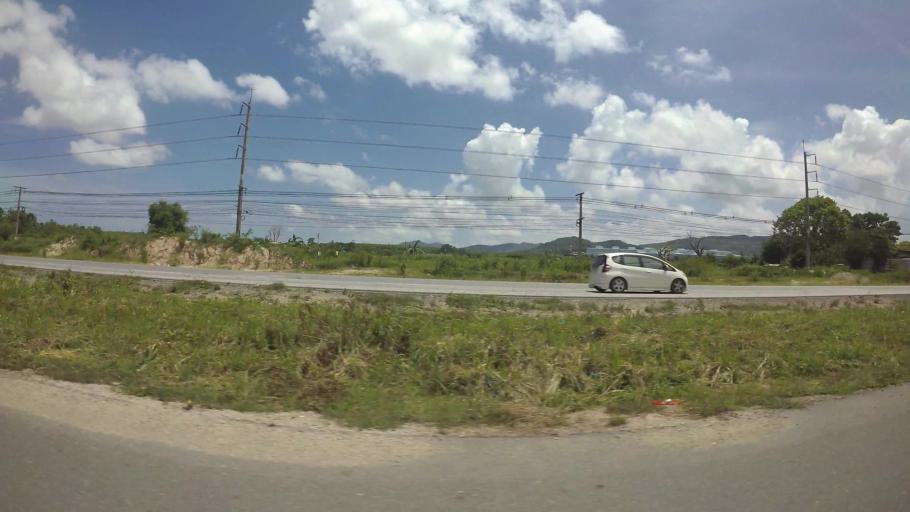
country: TH
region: Rayong
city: Nikhom Phattana
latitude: 12.8008
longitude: 101.1483
